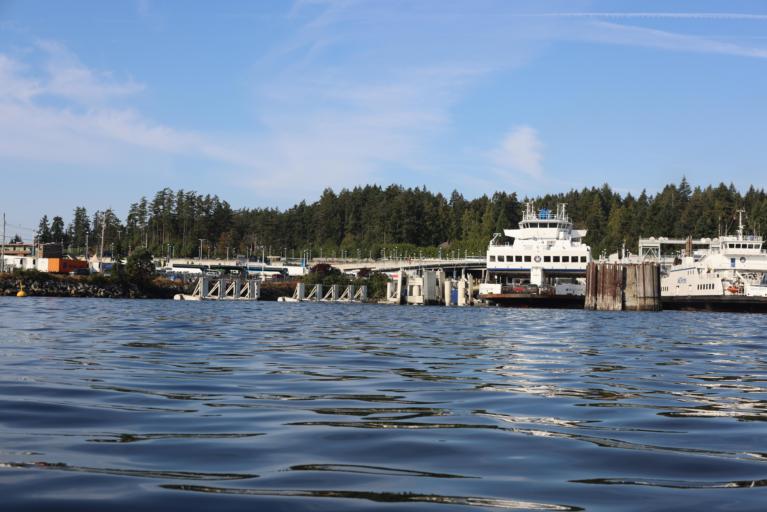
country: CA
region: British Columbia
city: North Saanich
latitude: 48.6903
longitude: -123.4072
